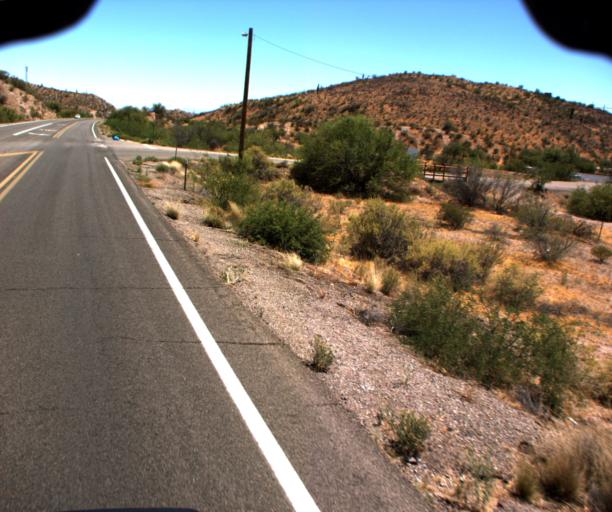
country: US
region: Arizona
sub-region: Pinal County
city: Kearny
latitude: 32.9517
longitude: -110.7444
